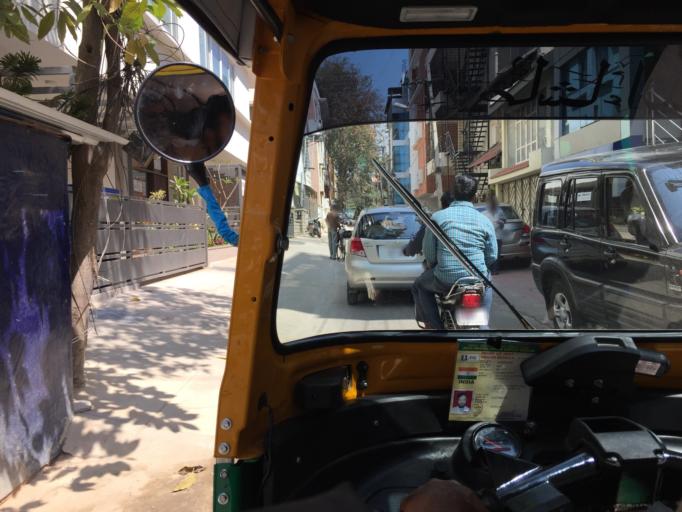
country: IN
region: Karnataka
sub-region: Bangalore Urban
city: Bangalore
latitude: 12.9780
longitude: 77.6394
